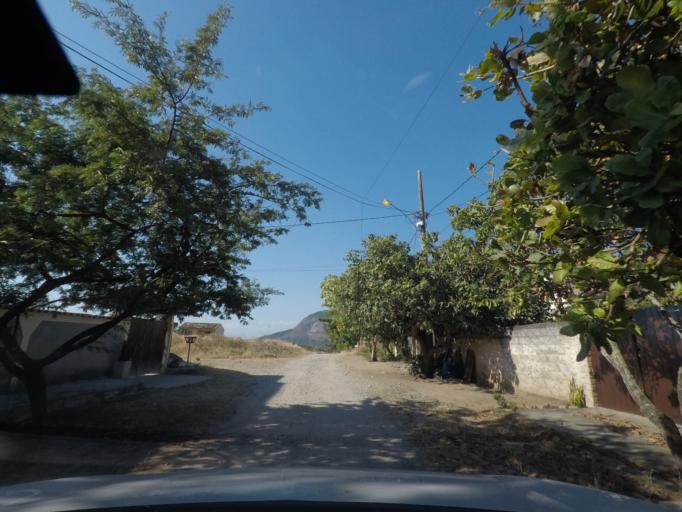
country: BR
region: Rio de Janeiro
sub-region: Marica
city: Marica
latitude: -22.9686
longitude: -42.9118
